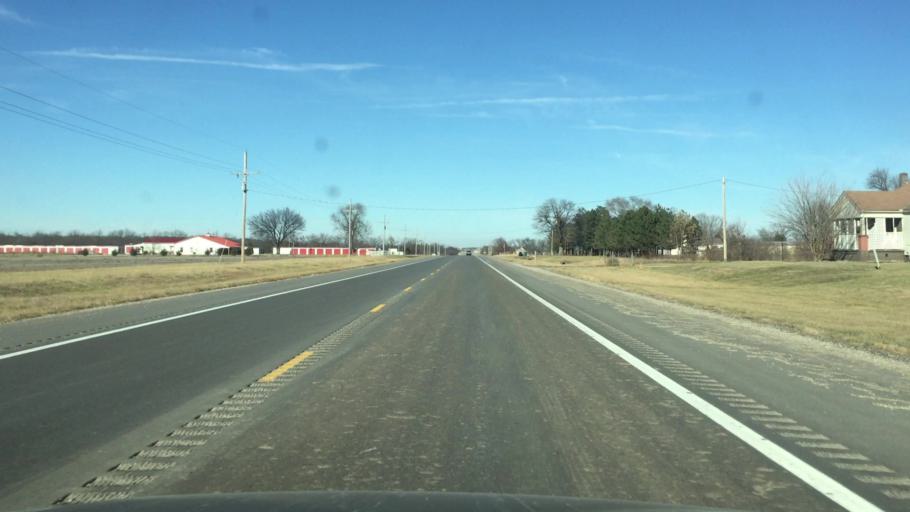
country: US
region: Kansas
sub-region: Franklin County
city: Ottawa
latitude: 38.5401
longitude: -95.2678
